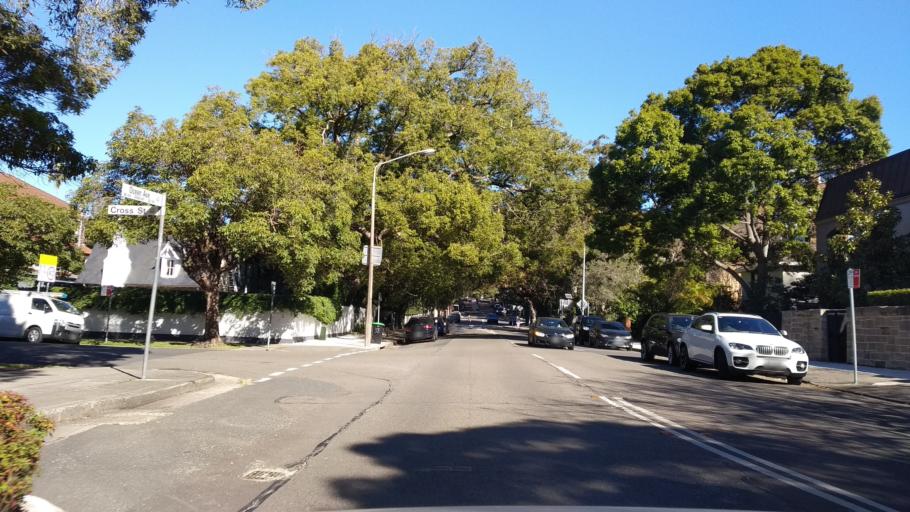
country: AU
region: New South Wales
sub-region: Woollahra
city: Darling Point
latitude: -33.8748
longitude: 151.2402
